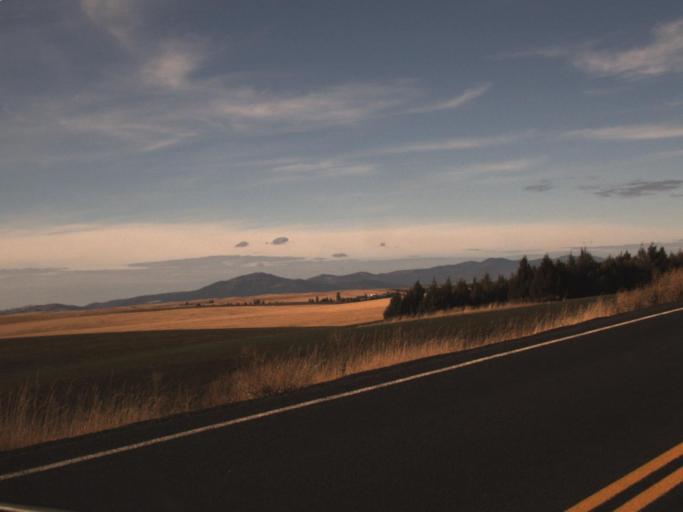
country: US
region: Washington
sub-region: Lincoln County
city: Davenport
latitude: 47.8342
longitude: -118.2118
